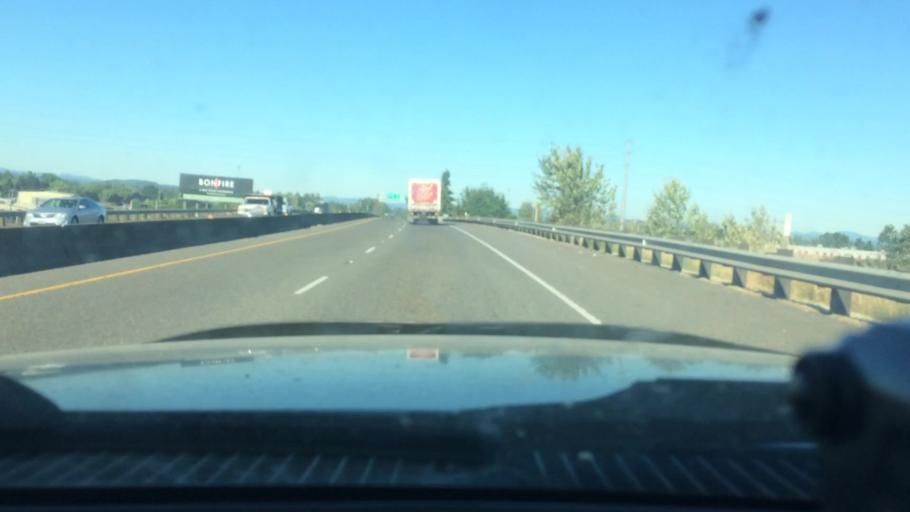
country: US
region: Oregon
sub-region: Lane County
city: Eugene
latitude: 44.0975
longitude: -123.1634
